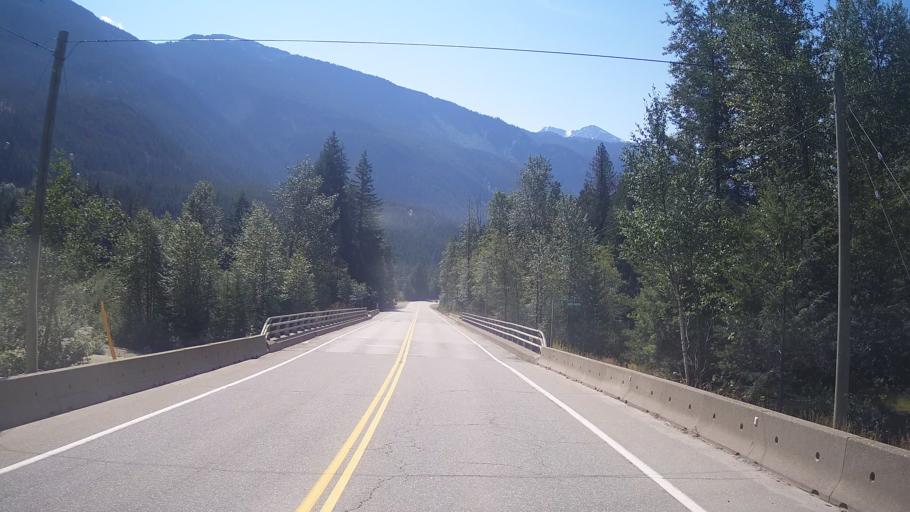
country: CA
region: British Columbia
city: Pemberton
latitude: 50.2587
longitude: -122.8641
